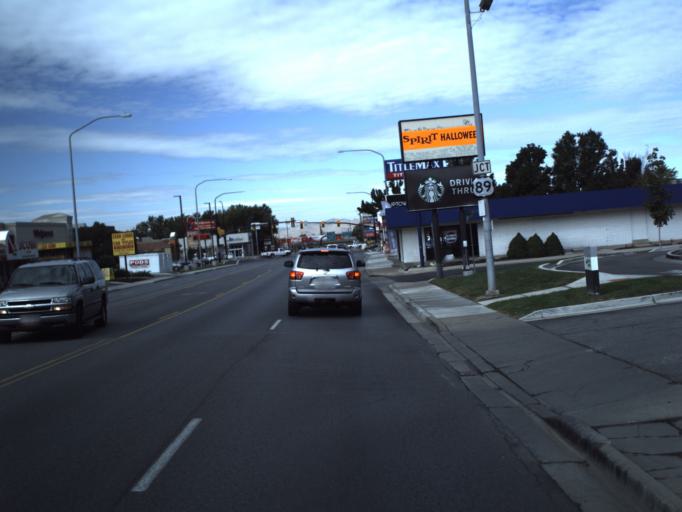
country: US
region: Utah
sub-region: Davis County
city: Bountiful
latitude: 40.8843
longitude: -111.8901
